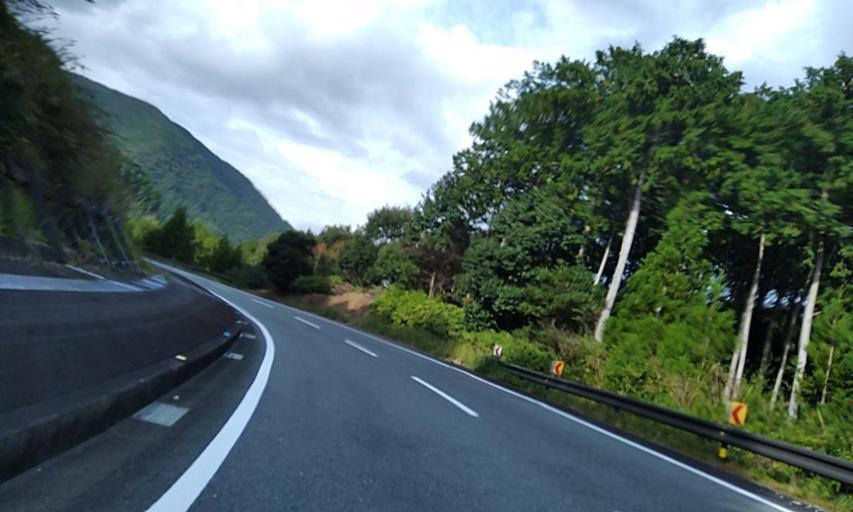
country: JP
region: Mie
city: Owase
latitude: 34.2368
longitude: 136.4002
